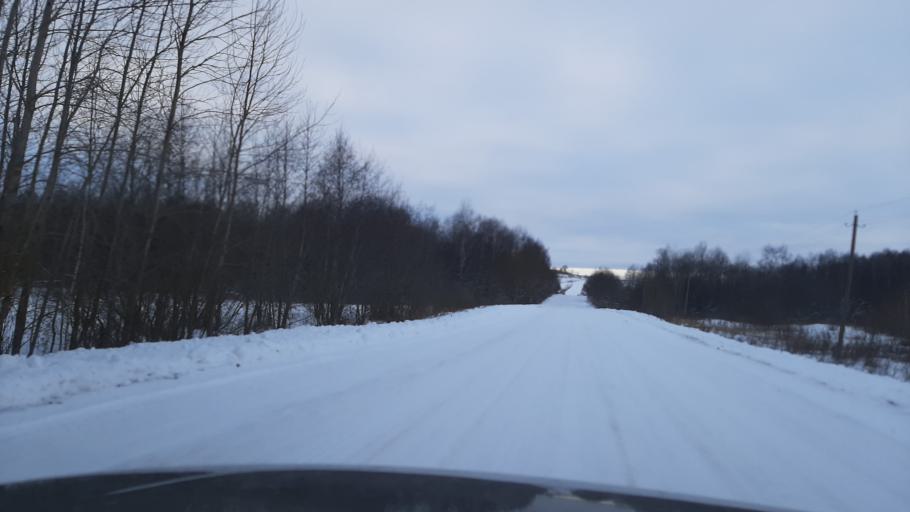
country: RU
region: Kostroma
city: Volgorechensk
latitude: 57.4449
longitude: 40.9536
